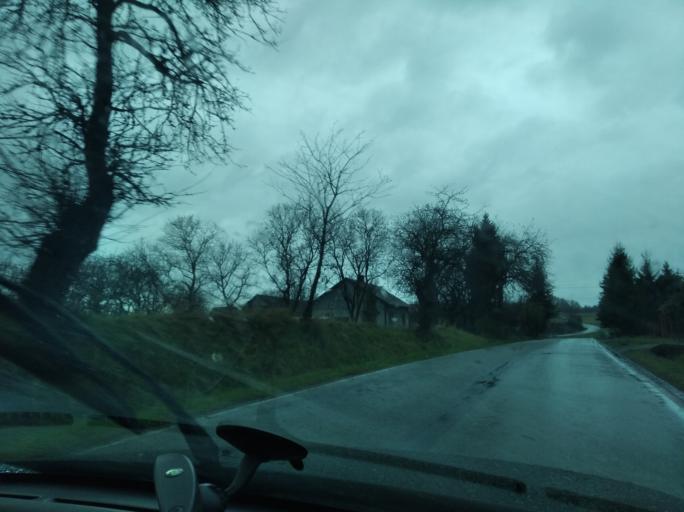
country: PL
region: Subcarpathian Voivodeship
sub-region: Powiat lancucki
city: Handzlowka
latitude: 49.9795
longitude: 22.1921
